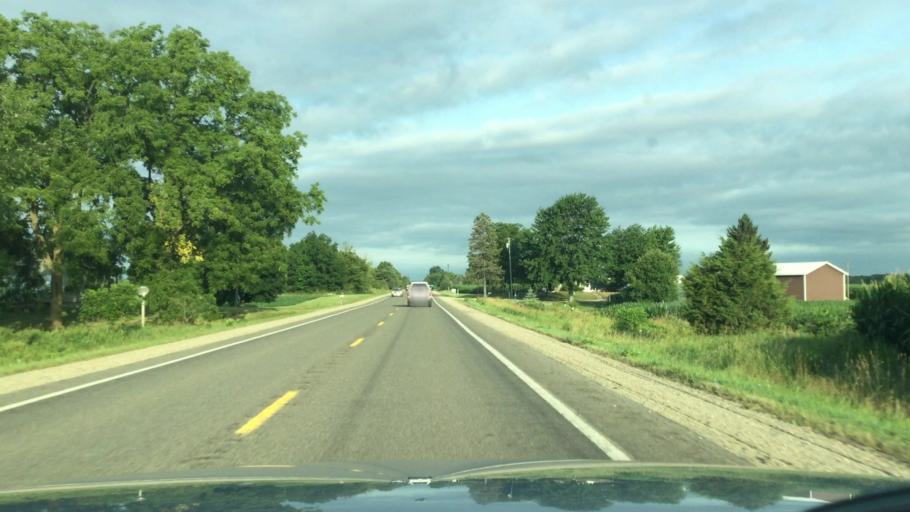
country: US
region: Michigan
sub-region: Montcalm County
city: Carson City
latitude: 43.1775
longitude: -84.9253
